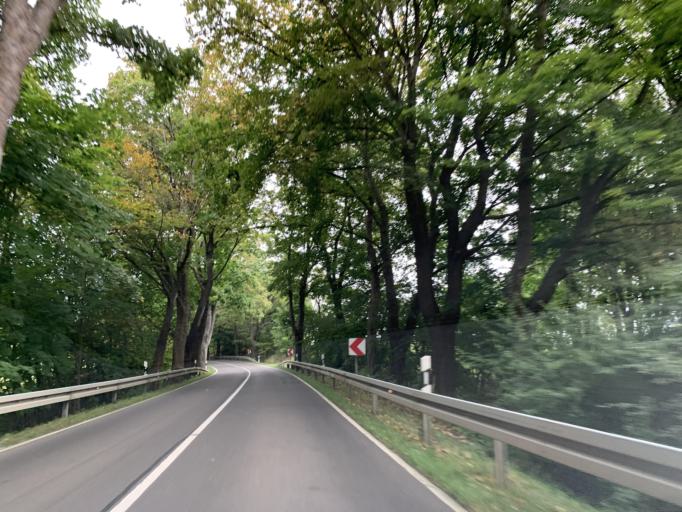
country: DE
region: Mecklenburg-Vorpommern
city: Loitz
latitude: 53.3336
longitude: 13.4905
